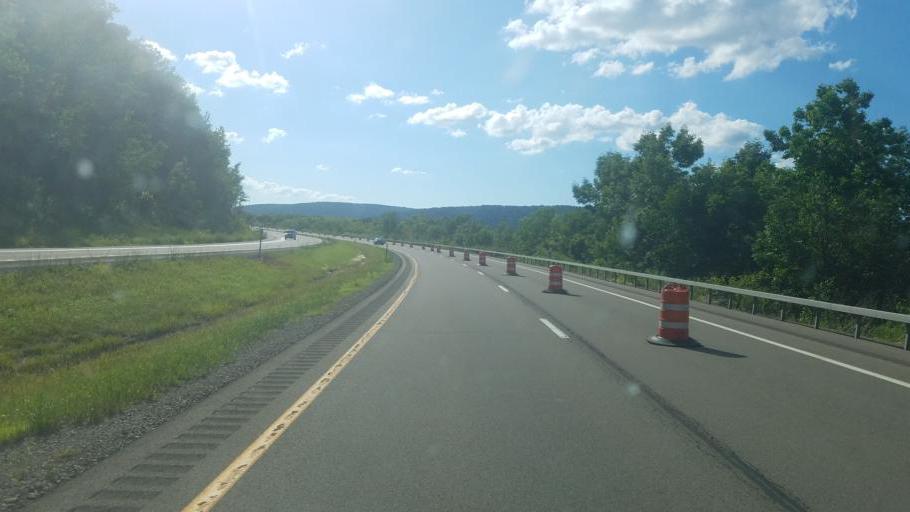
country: US
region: New York
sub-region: Cattaraugus County
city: Salamanca
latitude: 42.1039
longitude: -78.8192
